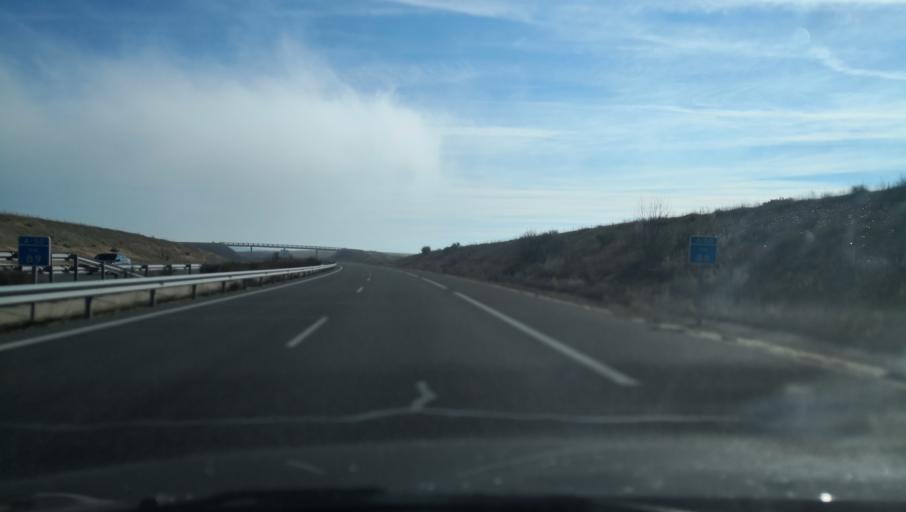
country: ES
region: Castille and Leon
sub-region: Provincia de Salamanca
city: Machacon
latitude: 40.9212
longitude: -5.5310
